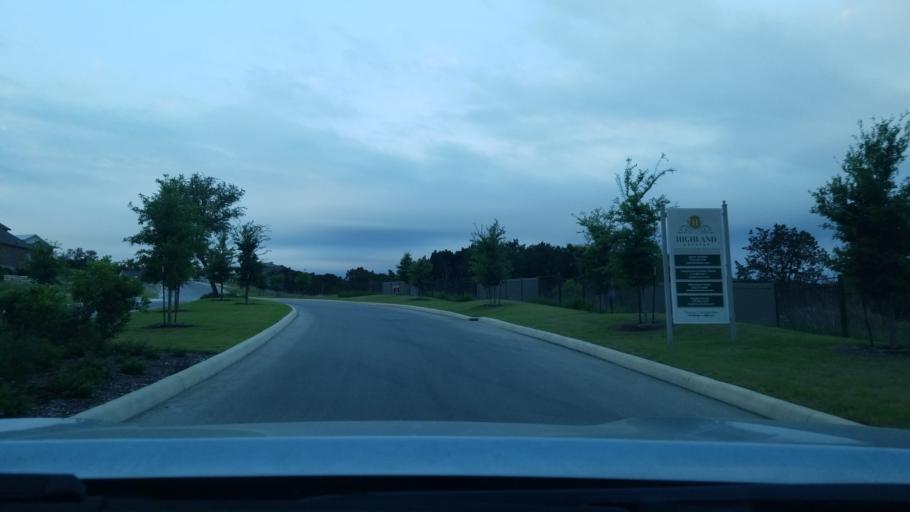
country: US
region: Texas
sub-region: Bexar County
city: Timberwood Park
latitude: 29.7119
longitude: -98.4679
